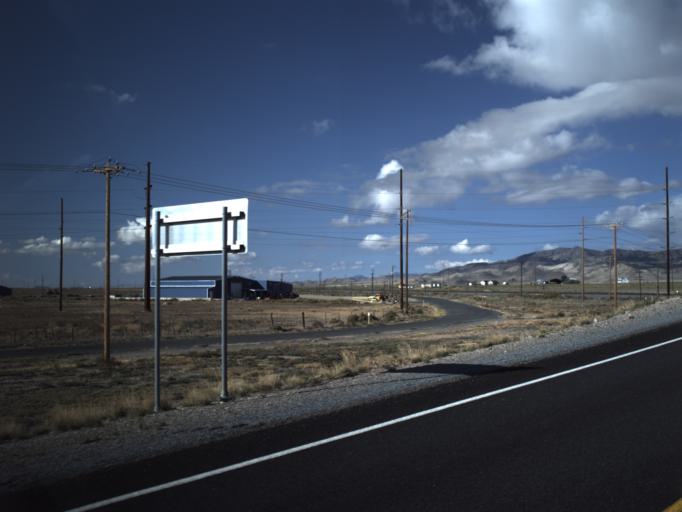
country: US
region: Utah
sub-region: Beaver County
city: Milford
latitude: 38.3868
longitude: -113.0123
